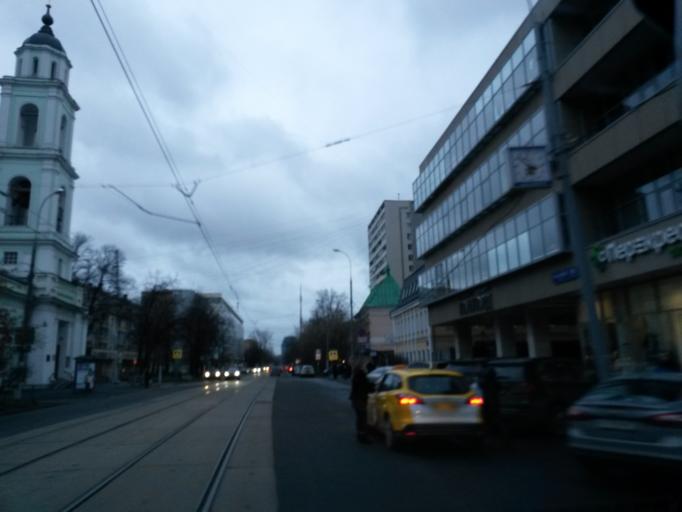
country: RU
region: Moscow
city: Zamoskvorech'ye
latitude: 55.7235
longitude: 37.6108
